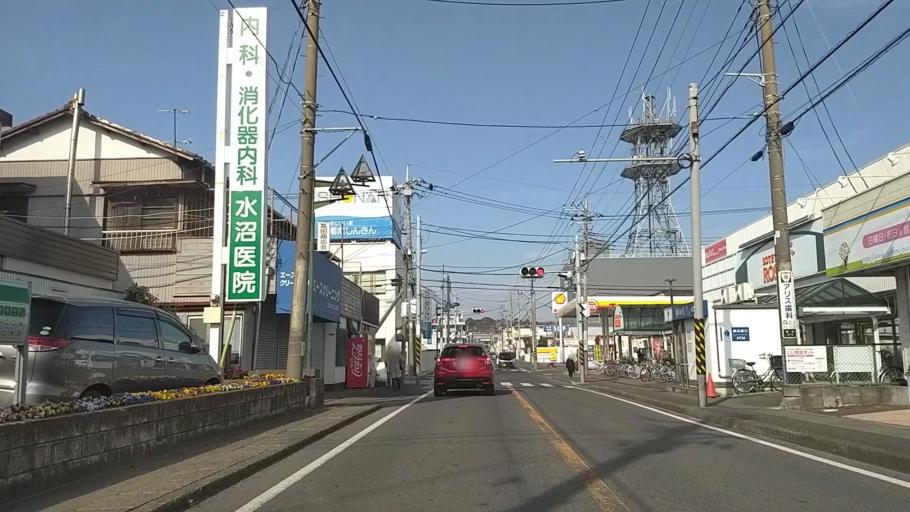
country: JP
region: Kanagawa
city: Chigasaki
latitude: 35.3454
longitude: 139.4127
